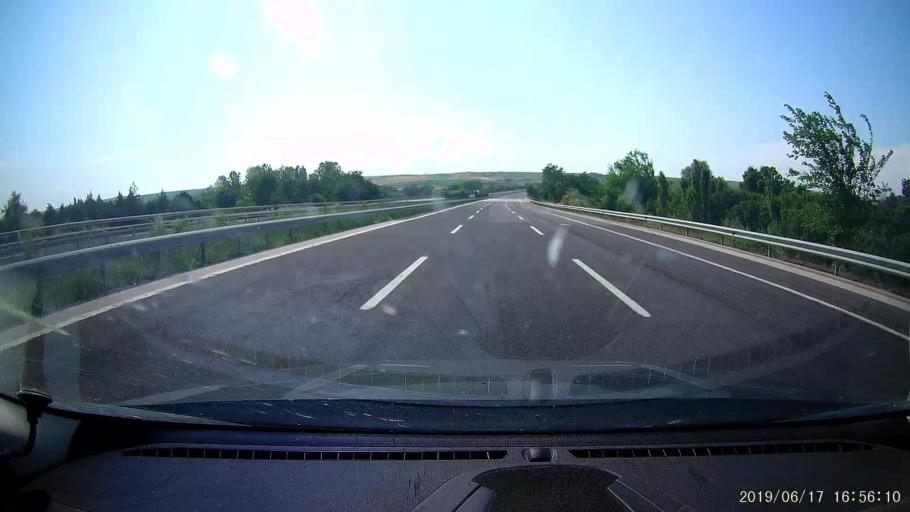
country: TR
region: Edirne
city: Haskoy
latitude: 41.5845
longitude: 26.9440
